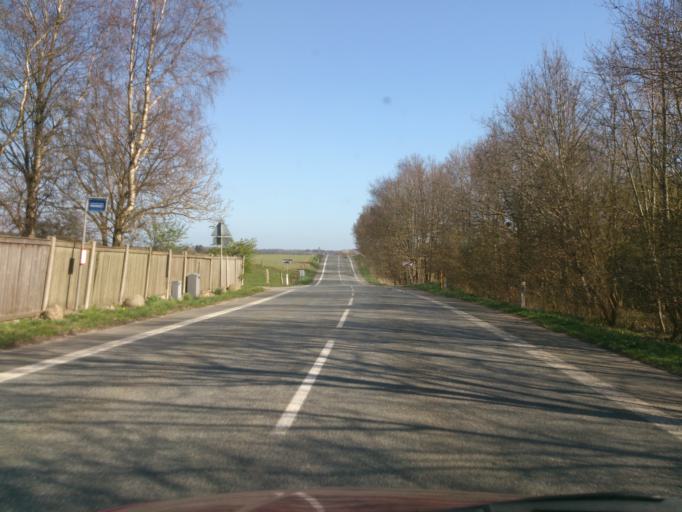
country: DK
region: Central Jutland
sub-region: Favrskov Kommune
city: Ulstrup
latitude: 56.4507
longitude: 9.7248
